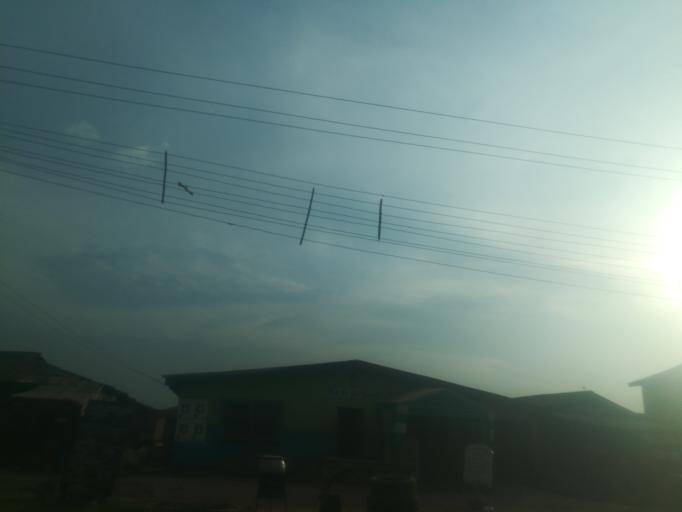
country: NG
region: Ogun
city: Abeokuta
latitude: 7.1693
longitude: 3.2958
